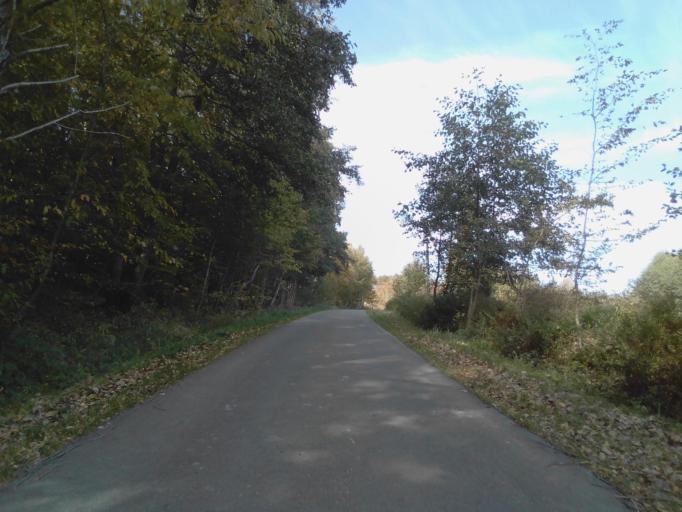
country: PL
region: Subcarpathian Voivodeship
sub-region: Powiat strzyzowski
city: Gwoznica Gorna
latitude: 49.8449
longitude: 21.9677
